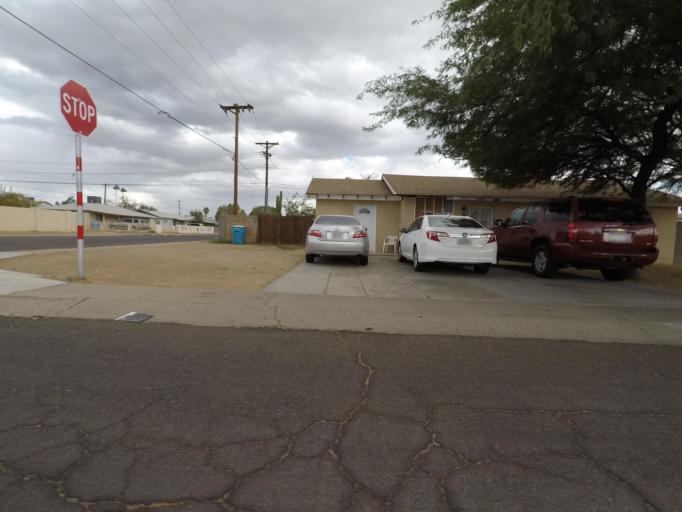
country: US
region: Arizona
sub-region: Maricopa County
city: Phoenix
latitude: 33.4985
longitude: -112.1246
